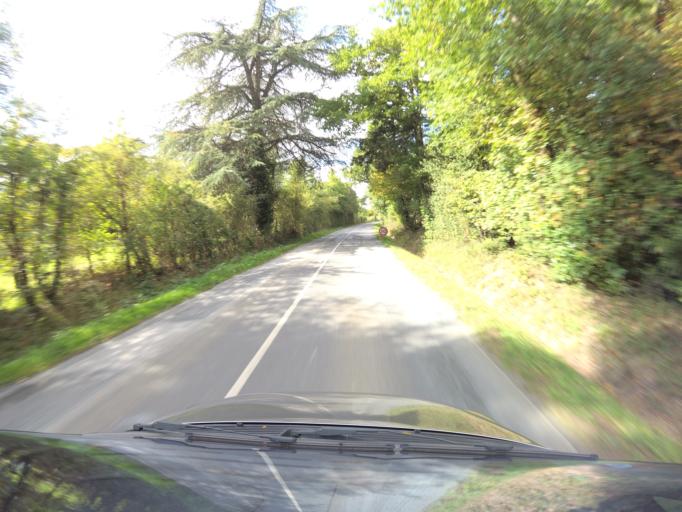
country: FR
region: Pays de la Loire
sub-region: Departement de la Loire-Atlantique
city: Casson
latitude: 47.4034
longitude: -1.5867
